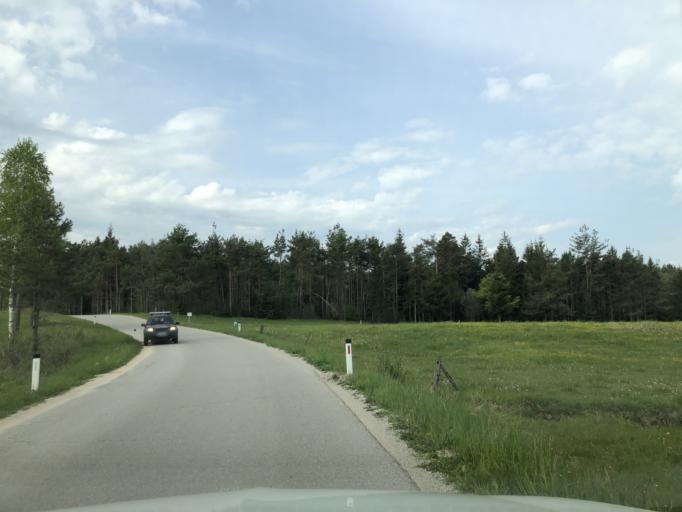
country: SI
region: Bloke
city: Nova Vas
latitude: 45.7902
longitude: 14.5009
